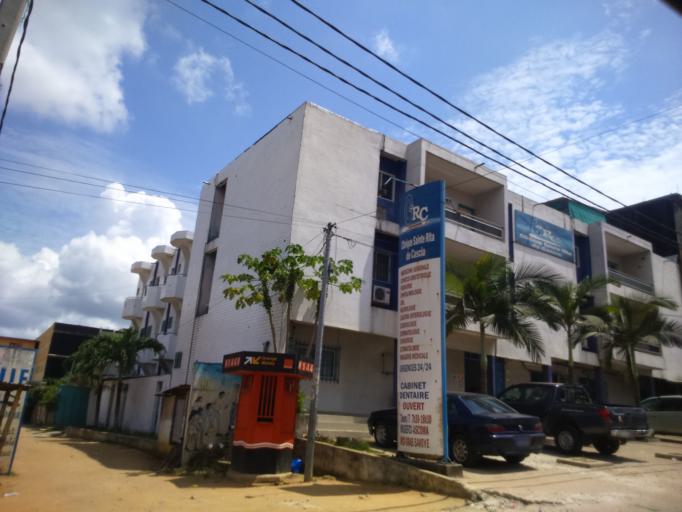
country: CI
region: Lagunes
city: Abidjan
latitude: 5.3406
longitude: -4.0875
